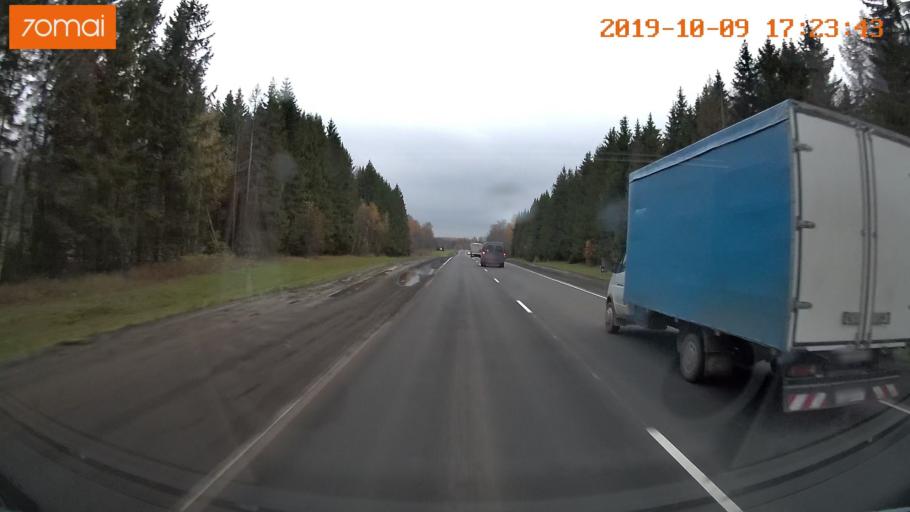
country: RU
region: Ivanovo
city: Furmanov
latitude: 57.1927
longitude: 41.1144
